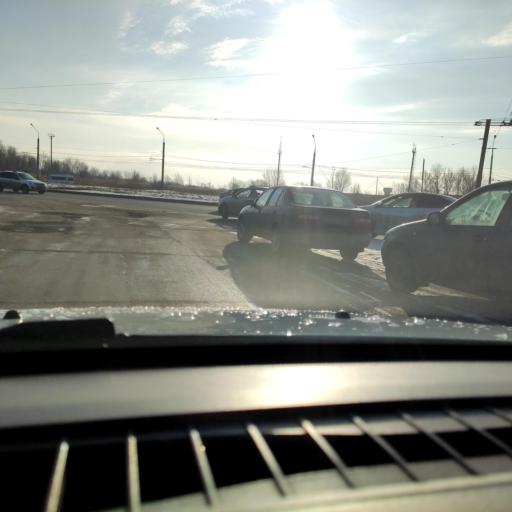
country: RU
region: Samara
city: Podstepki
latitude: 53.5591
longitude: 49.2260
